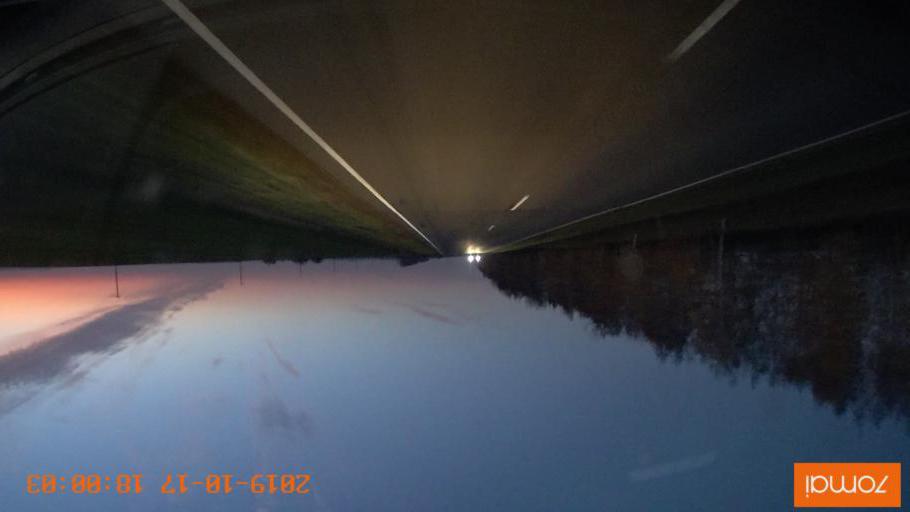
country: RU
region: Tula
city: Kurkino
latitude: 53.5278
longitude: 38.6179
